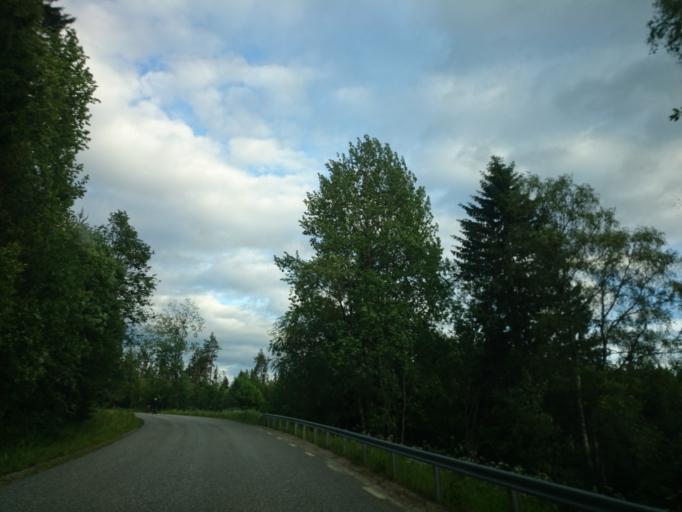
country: SE
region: Vaesternorrland
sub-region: Haernoesands Kommun
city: Haernoesand
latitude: 62.5803
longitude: 17.8173
